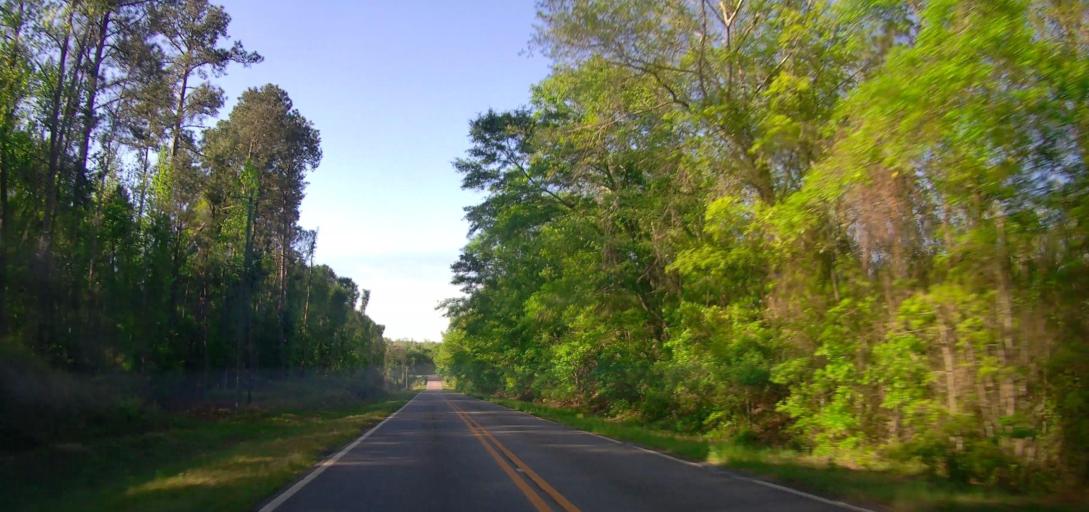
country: US
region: Georgia
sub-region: Houston County
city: Perry
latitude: 32.4572
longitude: -83.8171
